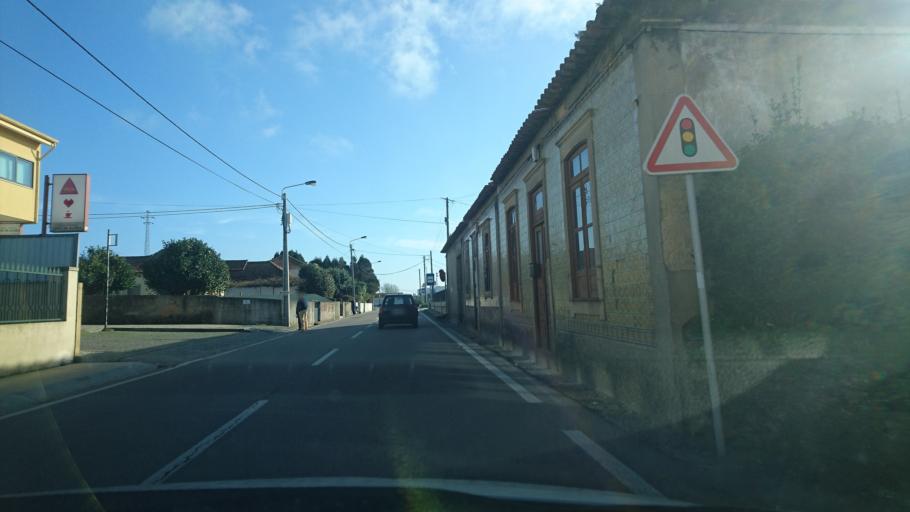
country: PT
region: Aveiro
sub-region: Ovar
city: Esmoriz
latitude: 40.9715
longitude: -8.6297
